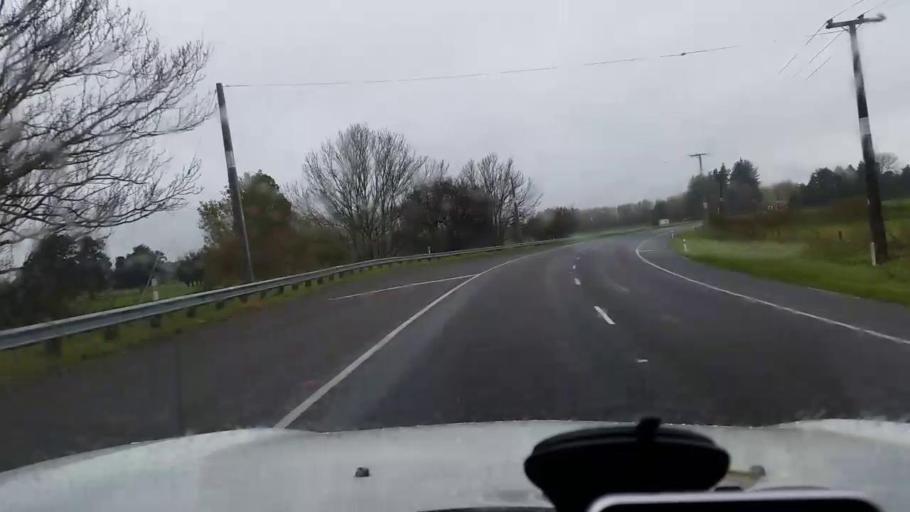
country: NZ
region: Wellington
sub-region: Masterton District
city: Masterton
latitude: -41.0683
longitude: 175.4739
